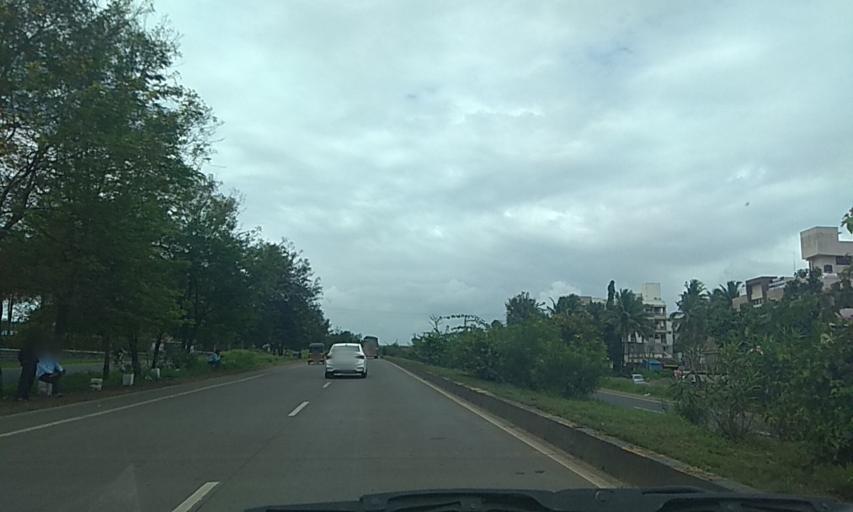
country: IN
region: Maharashtra
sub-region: Kolhapur
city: Kagal
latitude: 16.5875
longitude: 74.3088
